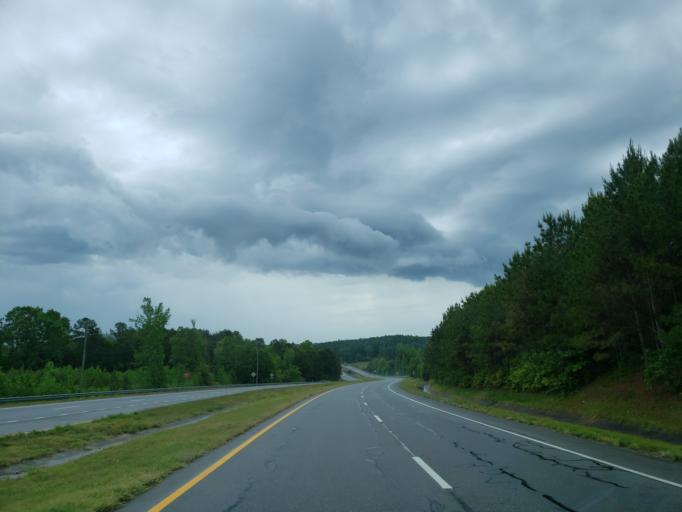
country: US
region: Georgia
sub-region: Haralson County
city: Buchanan
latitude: 33.8684
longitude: -85.2149
